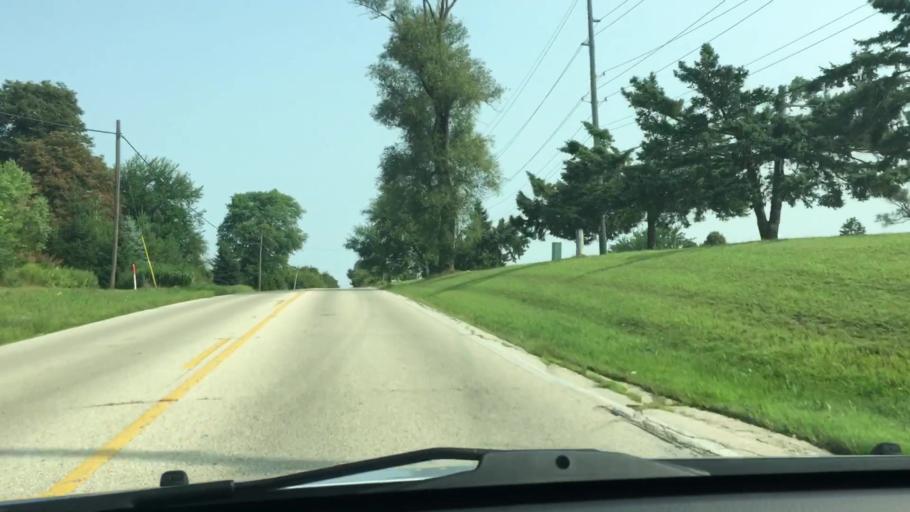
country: US
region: Wisconsin
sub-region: Waukesha County
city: Oconomowoc
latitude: 43.0857
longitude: -88.4956
